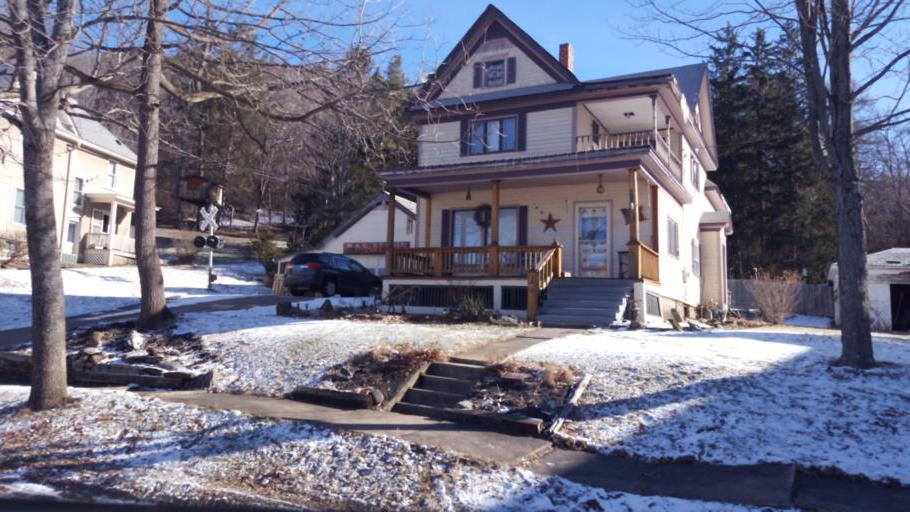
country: US
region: New York
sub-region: Allegany County
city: Wellsville
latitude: 42.1263
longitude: -77.9466
